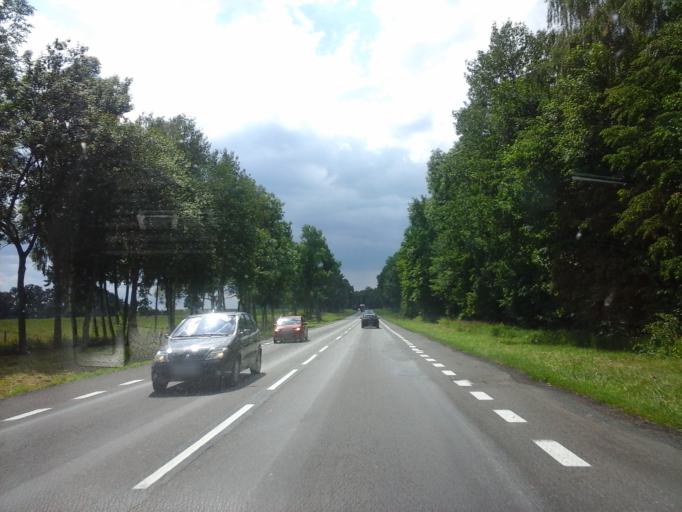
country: PL
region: West Pomeranian Voivodeship
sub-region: Powiat bialogardzki
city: Karlino
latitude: 54.0209
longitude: 15.8401
